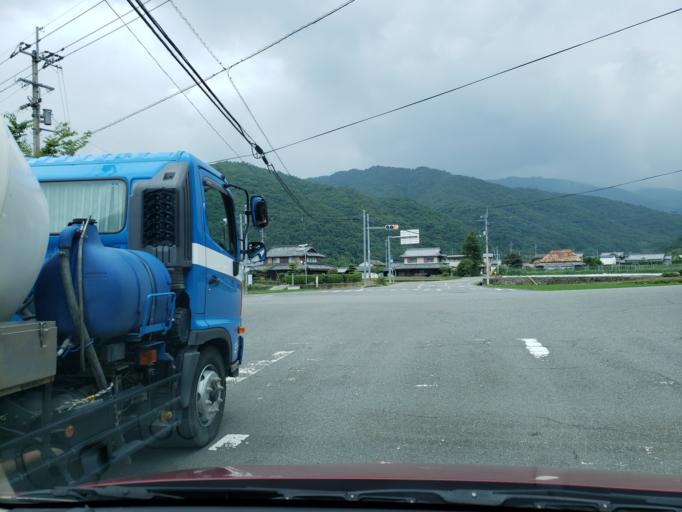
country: JP
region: Tokushima
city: Wakimachi
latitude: 34.1010
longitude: 134.2260
